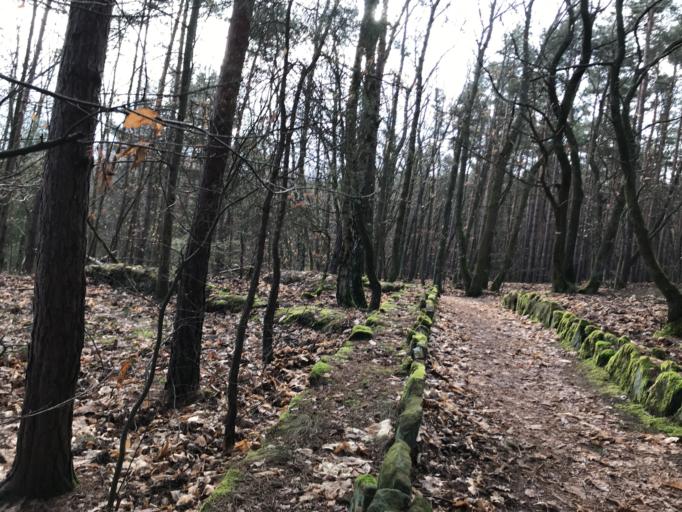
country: DE
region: Rheinland-Pfalz
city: Bad Duerkheim
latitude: 49.4473
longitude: 8.1581
